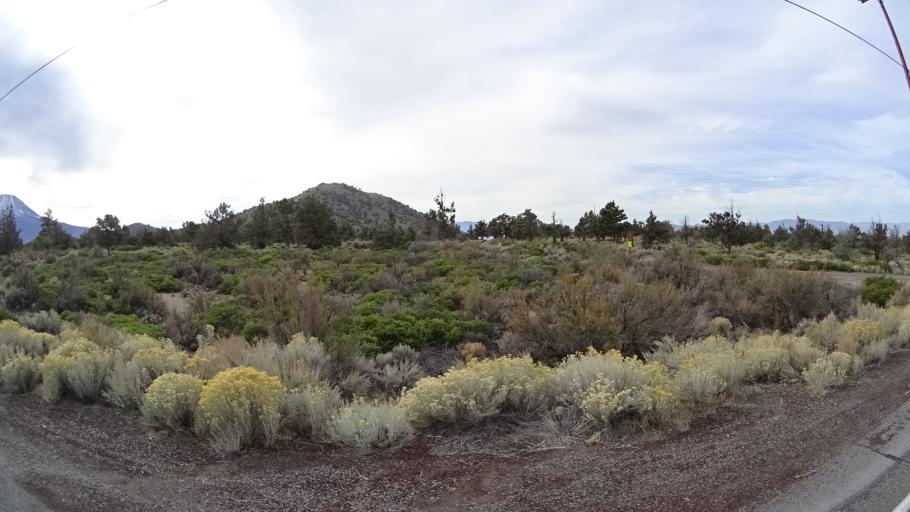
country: US
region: California
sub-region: Siskiyou County
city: Weed
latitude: 41.5556
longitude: -122.2544
